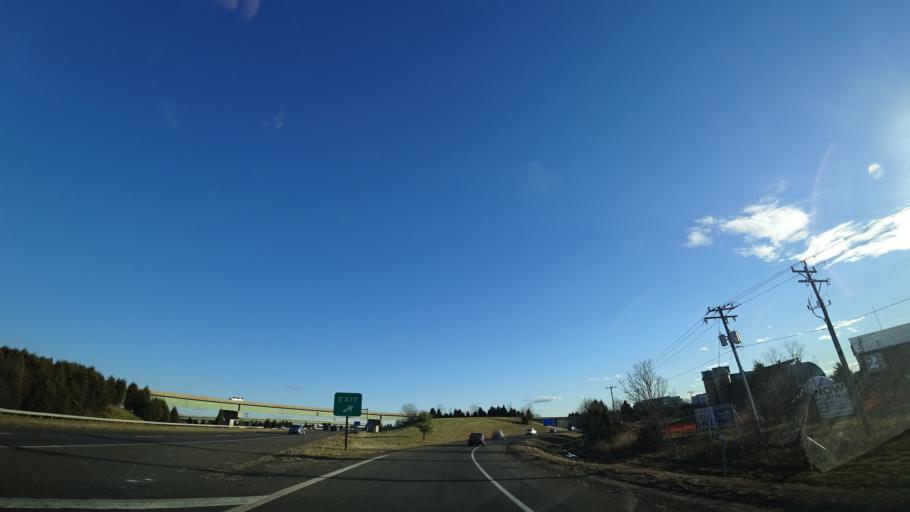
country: US
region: Virginia
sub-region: Prince William County
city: Bull Run
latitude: 38.7439
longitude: -77.5213
